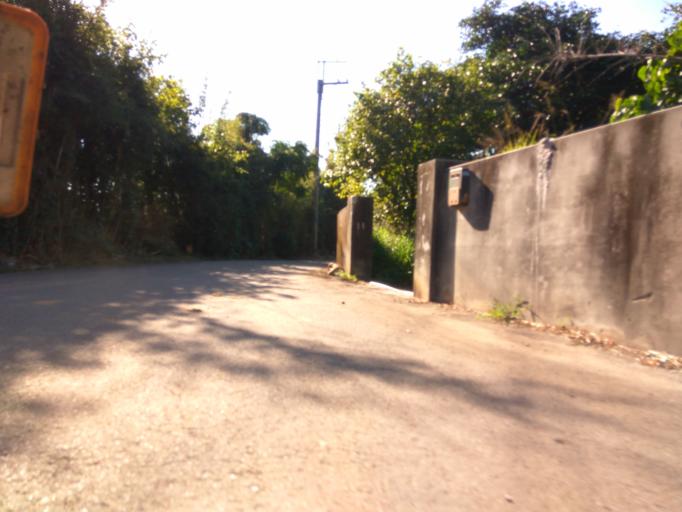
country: TW
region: Taiwan
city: Taoyuan City
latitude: 24.9781
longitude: 121.1840
